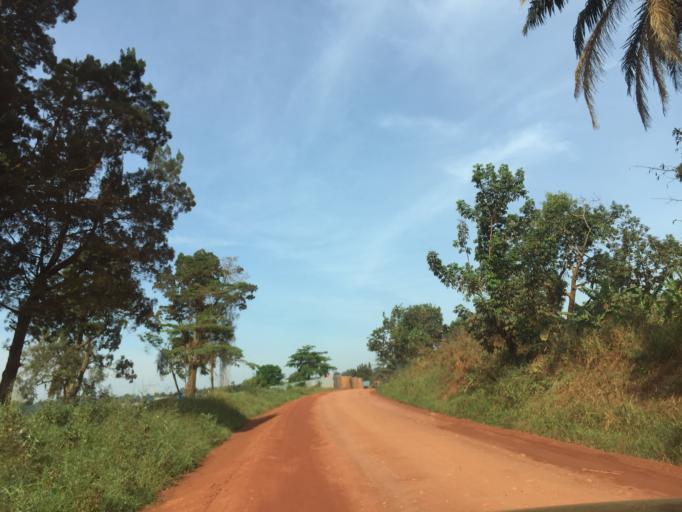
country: UG
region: Central Region
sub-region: Wakiso District
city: Wakiso
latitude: 0.4626
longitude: 32.5503
